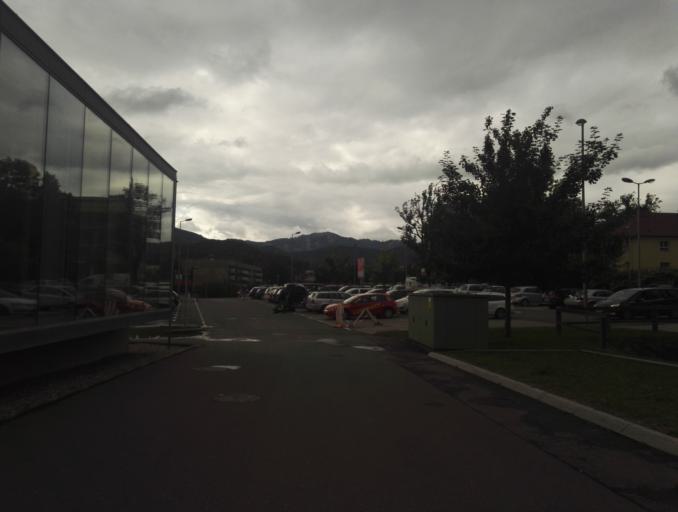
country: AT
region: Styria
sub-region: Politischer Bezirk Leoben
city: Leoben
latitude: 47.3878
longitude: 15.0955
